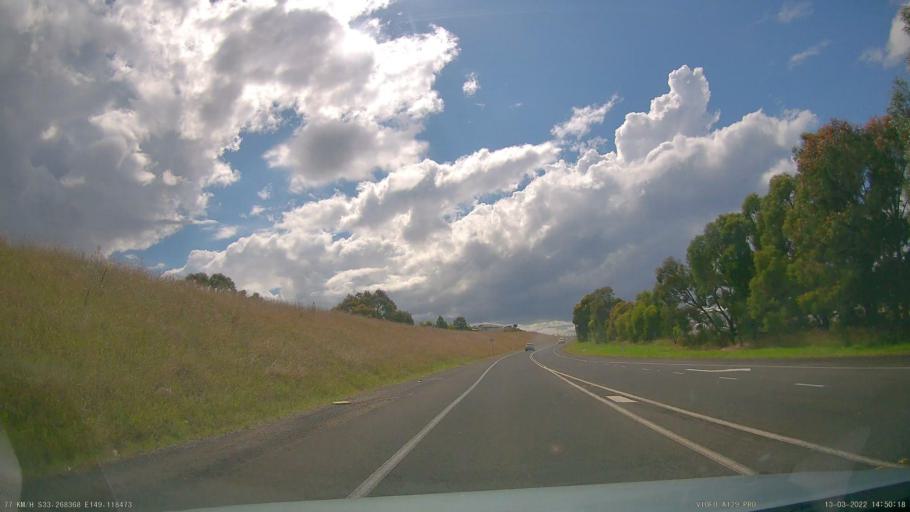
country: AU
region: New South Wales
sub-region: Orange Municipality
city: Orange
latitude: -33.2682
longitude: 149.1184
